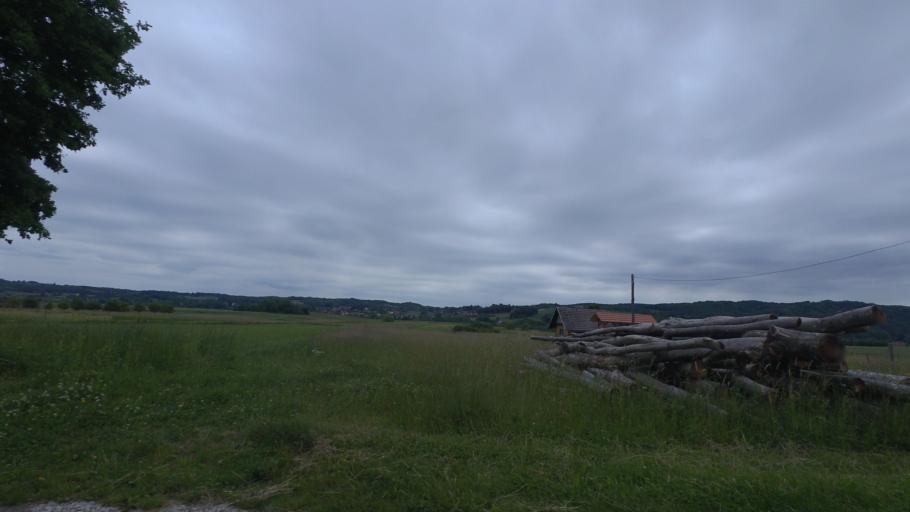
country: HR
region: Karlovacka
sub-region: Grad Karlovac
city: Karlovac
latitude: 45.4133
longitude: 15.5933
